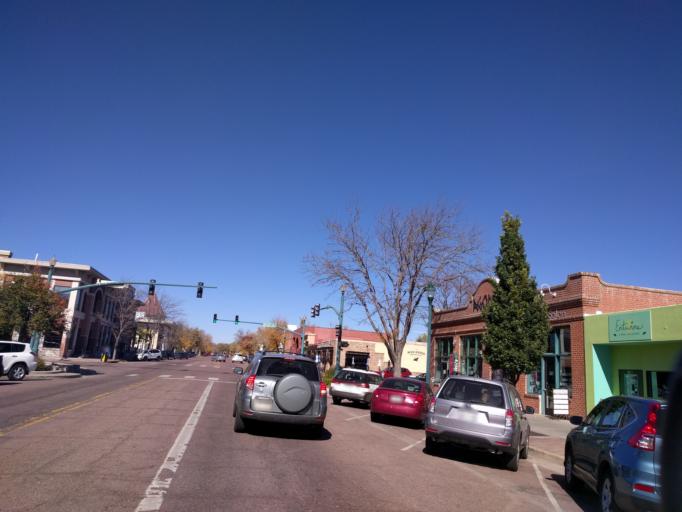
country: US
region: Colorado
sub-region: El Paso County
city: Colorado Springs
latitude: 38.8391
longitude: -104.8232
